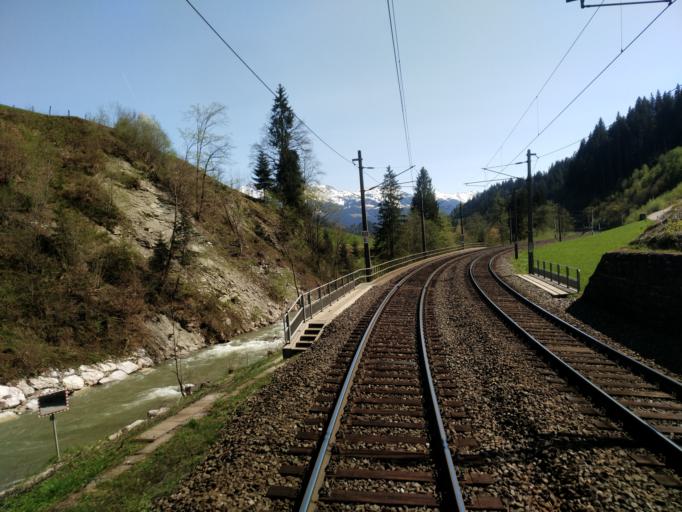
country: AT
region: Tyrol
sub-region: Politischer Bezirk Kitzbuhel
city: Hopfgarten im Brixental
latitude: 47.4370
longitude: 12.1726
